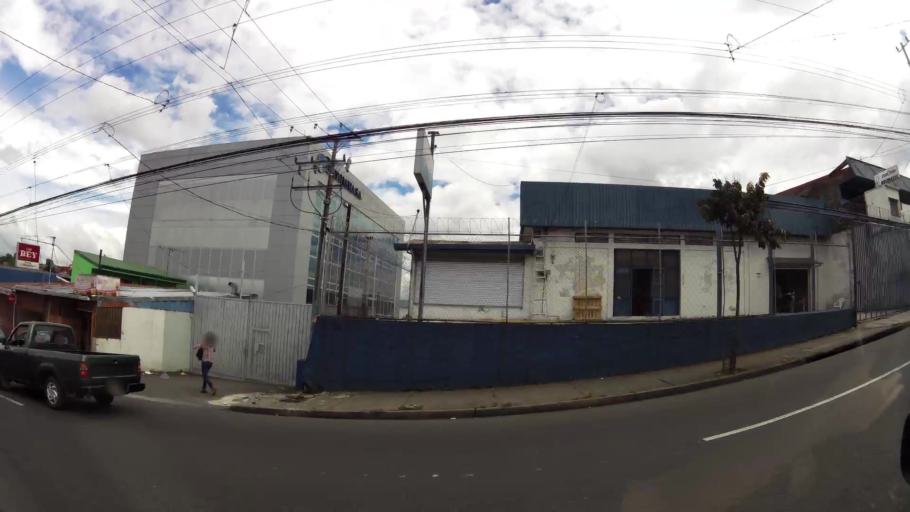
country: CR
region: San Jose
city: San Jose
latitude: 9.9155
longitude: -84.0845
